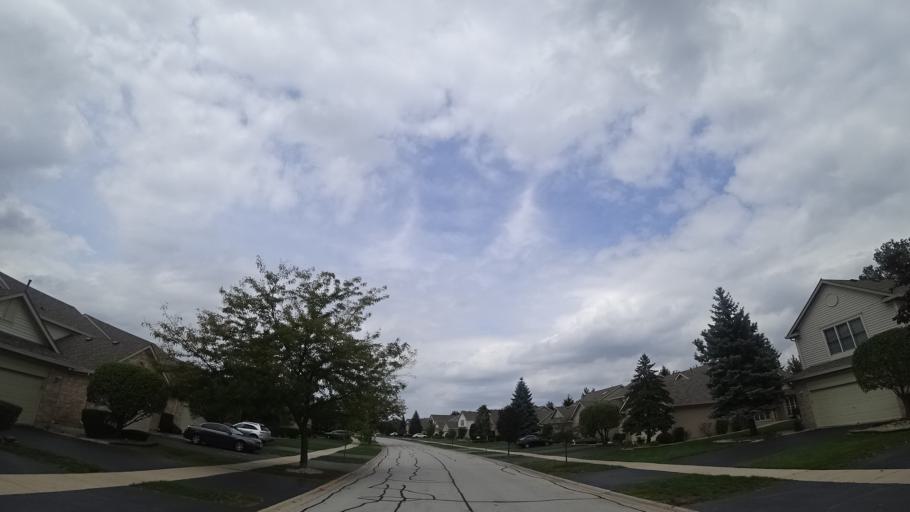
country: US
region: Illinois
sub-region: Cook County
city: Tinley Park
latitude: 41.5699
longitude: -87.8042
